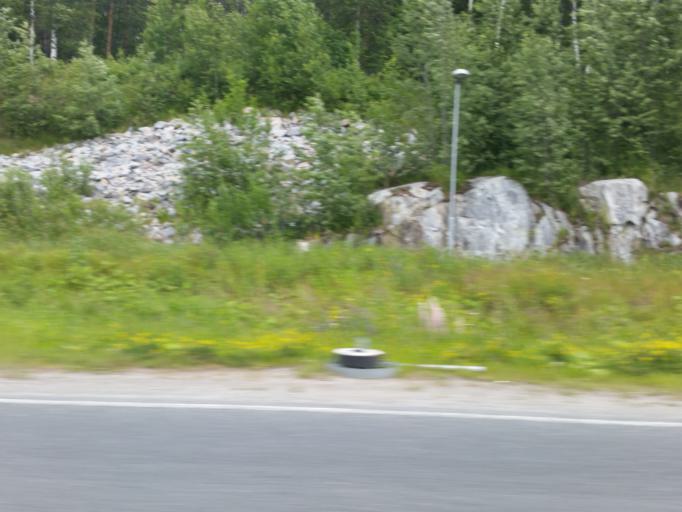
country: FI
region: Northern Savo
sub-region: Kuopio
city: Kuopio
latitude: 62.8843
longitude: 27.6420
